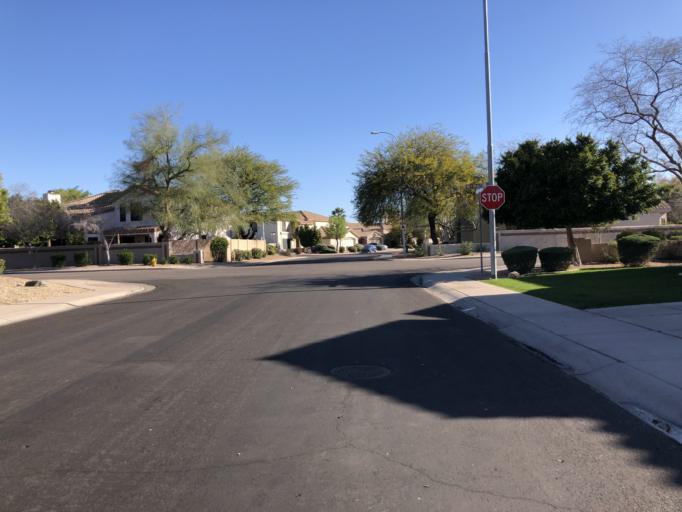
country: US
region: Arizona
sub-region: Maricopa County
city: San Carlos
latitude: 33.3157
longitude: -111.9134
